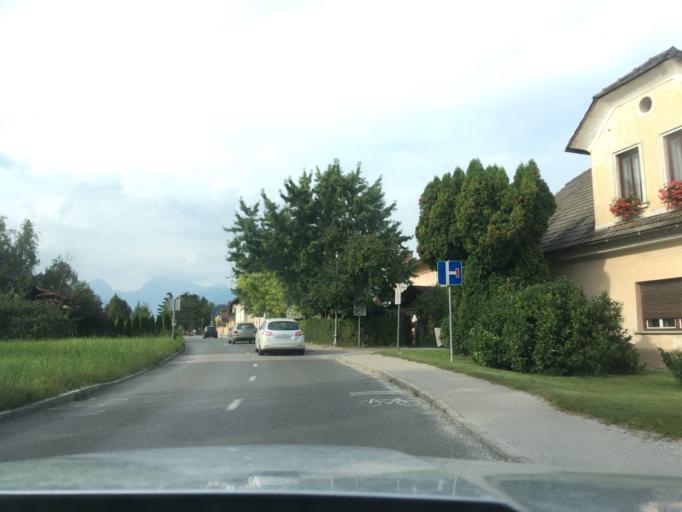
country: SI
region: Domzale
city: Radomlje
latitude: 46.1751
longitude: 14.6102
